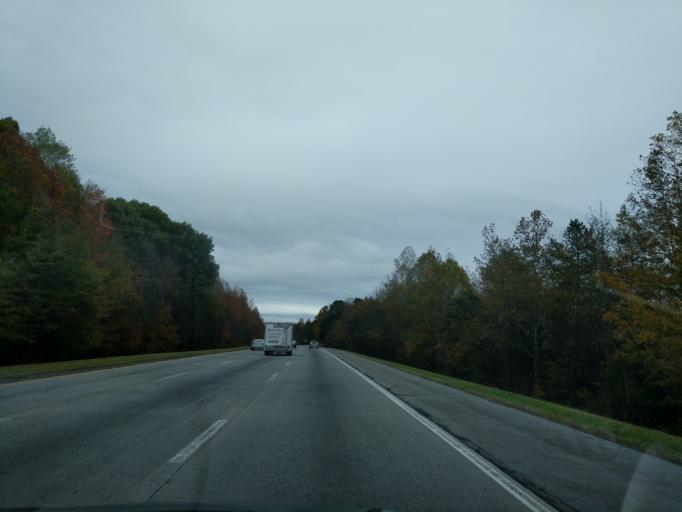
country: US
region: North Carolina
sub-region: Davidson County
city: Thomasville
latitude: 35.8332
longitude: -80.1483
